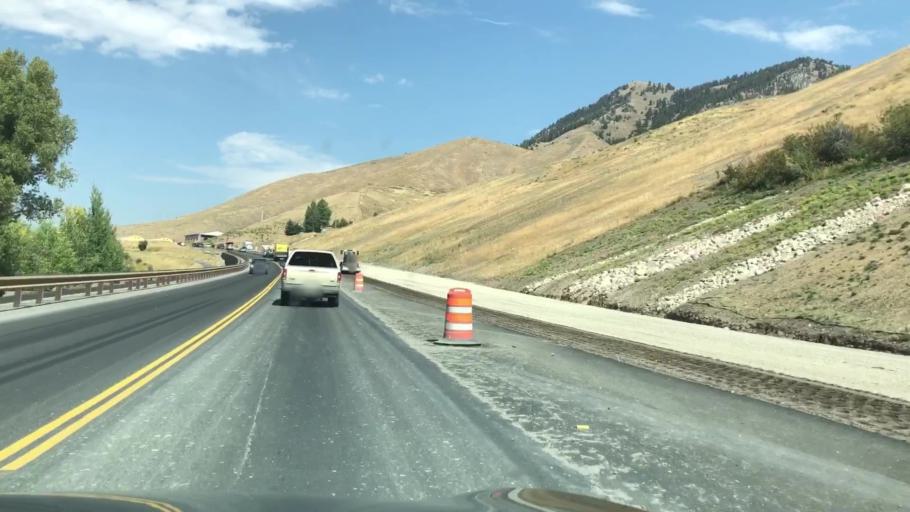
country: US
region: Wyoming
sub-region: Teton County
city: South Park
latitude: 43.3962
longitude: -110.7492
